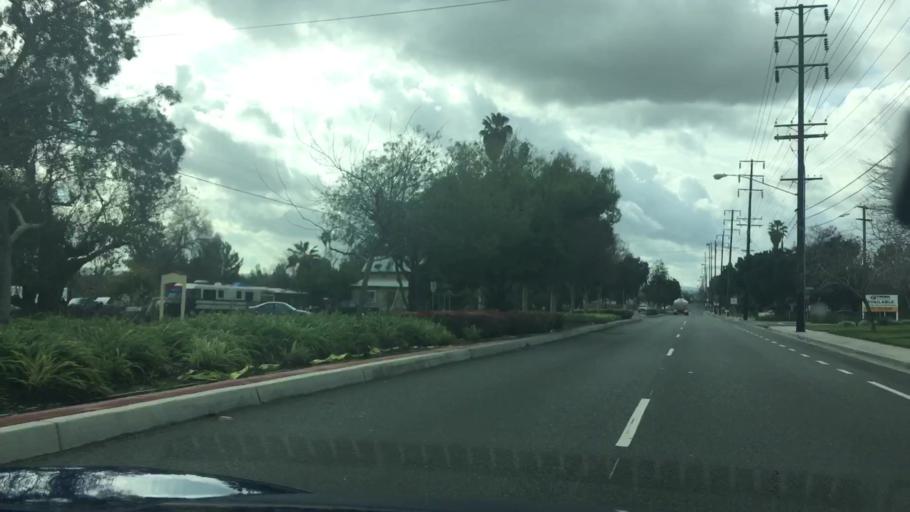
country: US
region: California
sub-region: Riverside County
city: Highgrove
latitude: 34.0104
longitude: -117.3635
